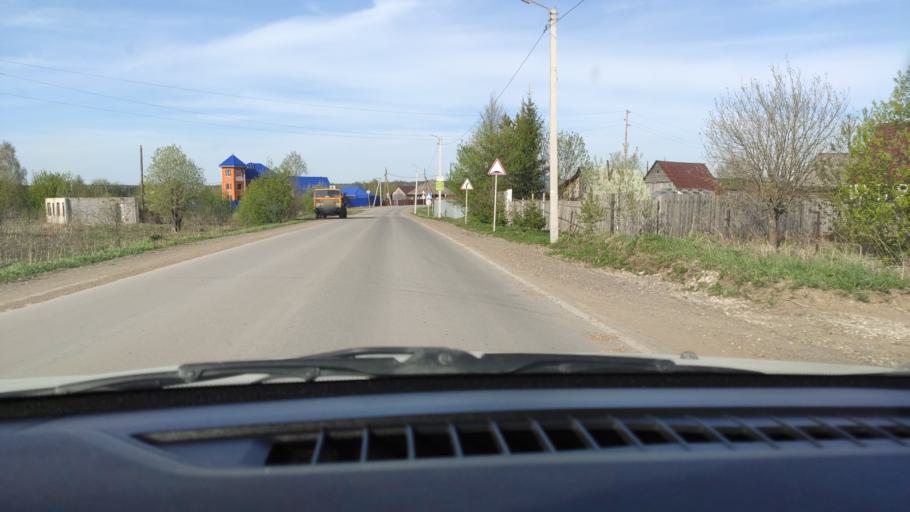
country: RU
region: Perm
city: Sylva
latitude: 57.9304
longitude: 56.6907
